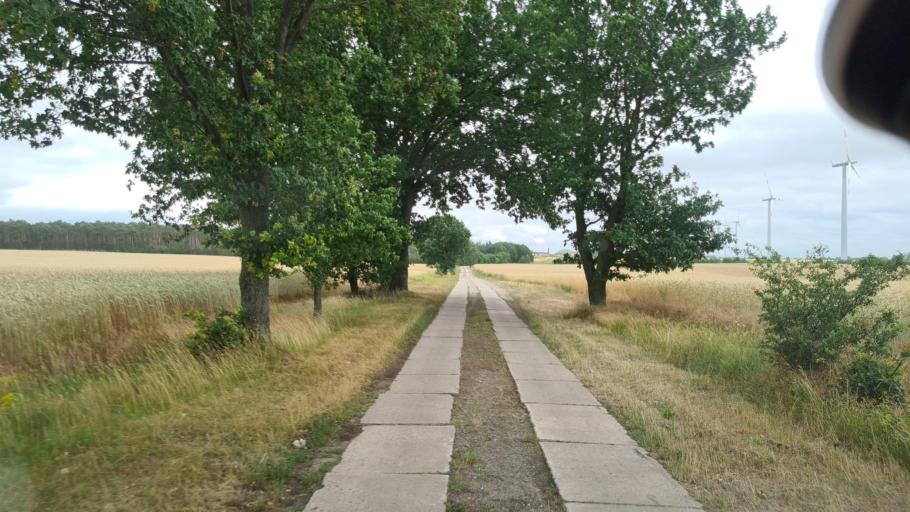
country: DE
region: Brandenburg
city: Juterbog
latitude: 51.9601
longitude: 13.1756
